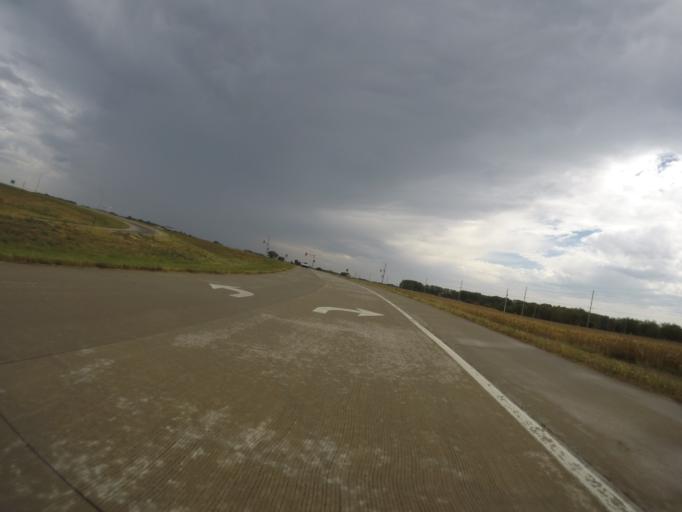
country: US
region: Kansas
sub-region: Riley County
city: Ogden
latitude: 39.1120
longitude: -96.6944
